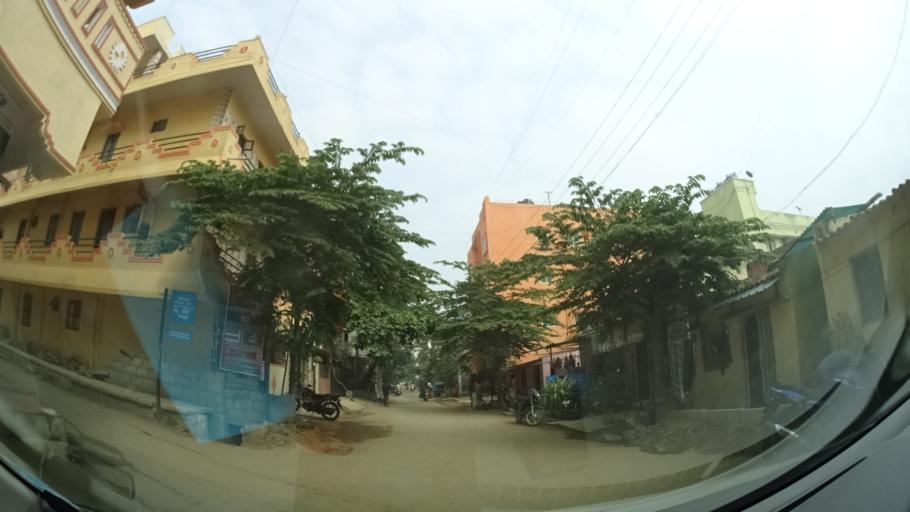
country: IN
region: Karnataka
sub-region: Bangalore Rural
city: Hoskote
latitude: 12.9715
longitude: 77.7532
